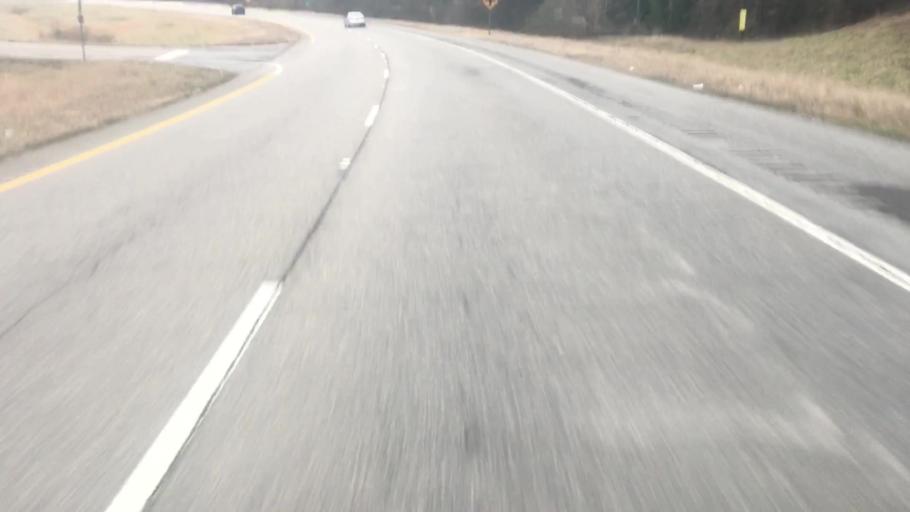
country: US
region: Alabama
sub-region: Walker County
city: Cordova
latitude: 33.8084
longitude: -87.1461
